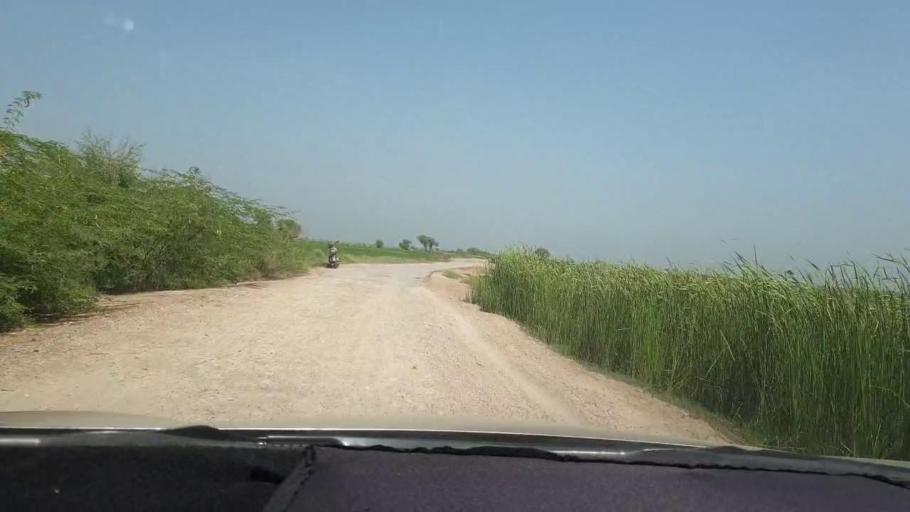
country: PK
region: Sindh
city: Shahdadkot
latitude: 27.8307
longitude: 67.9903
